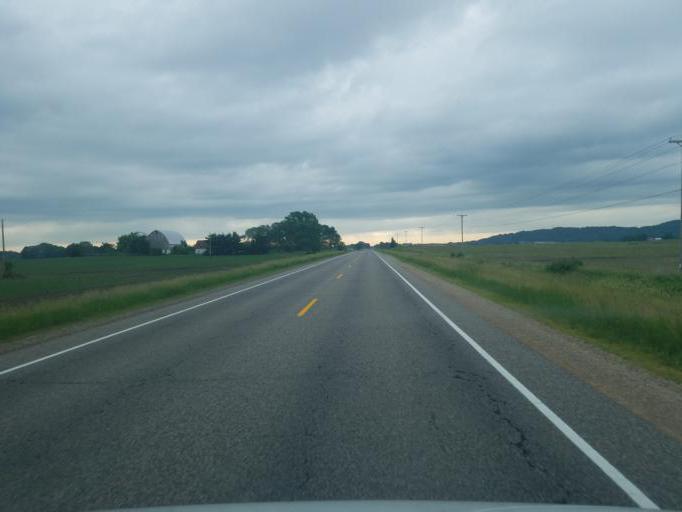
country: US
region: Wisconsin
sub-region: Juneau County
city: Mauston
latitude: 43.7891
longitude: -90.1053
